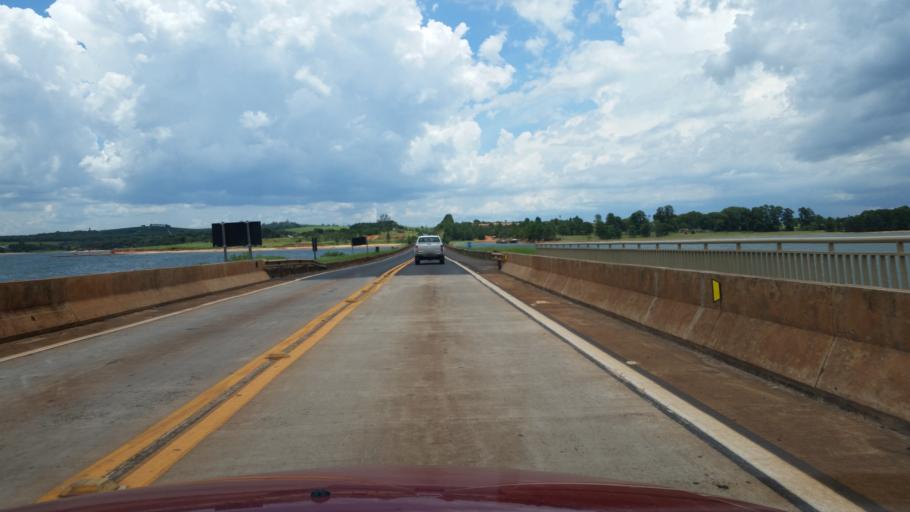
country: BR
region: Sao Paulo
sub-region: Itai
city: Itai
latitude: -23.2687
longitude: -49.0100
